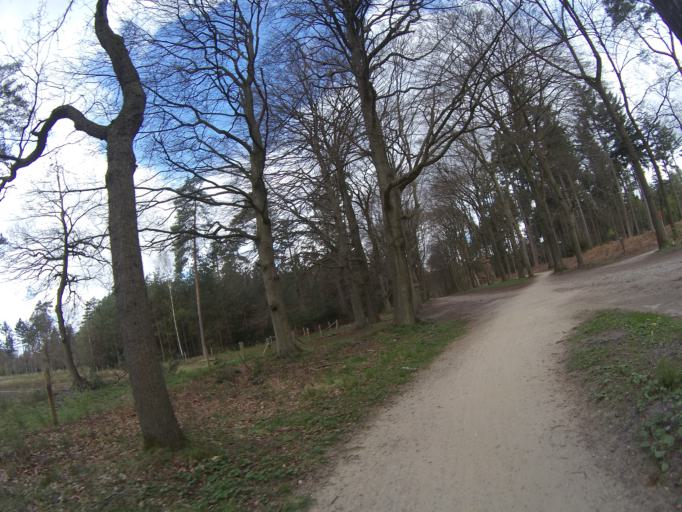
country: NL
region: Utrecht
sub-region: Gemeente Soest
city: Soest
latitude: 52.1792
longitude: 5.2369
